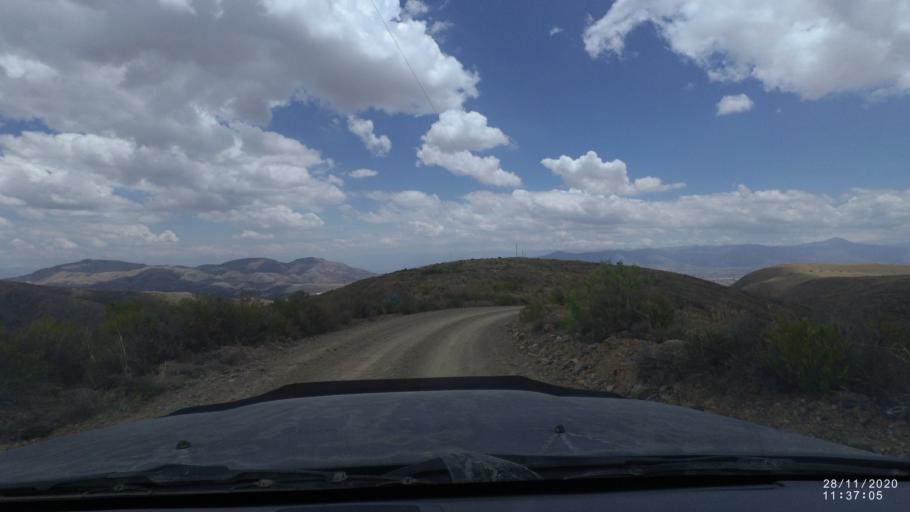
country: BO
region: Cochabamba
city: Tarata
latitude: -17.6808
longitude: -66.0433
